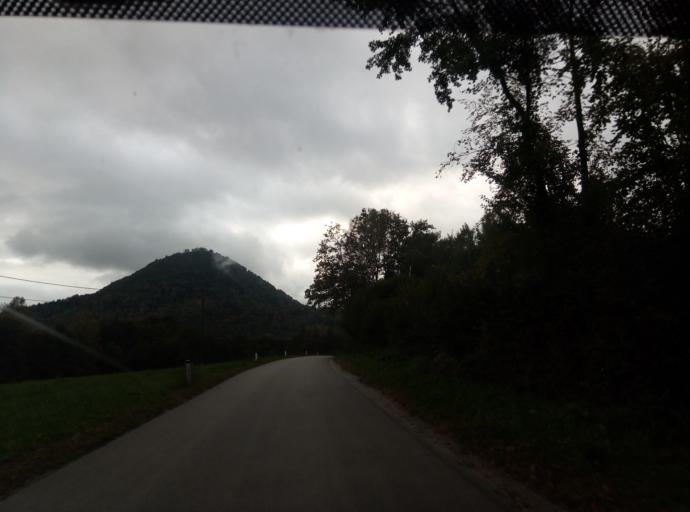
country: SI
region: Medvode
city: Zgornje Pirnice
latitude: 46.1303
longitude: 14.4875
